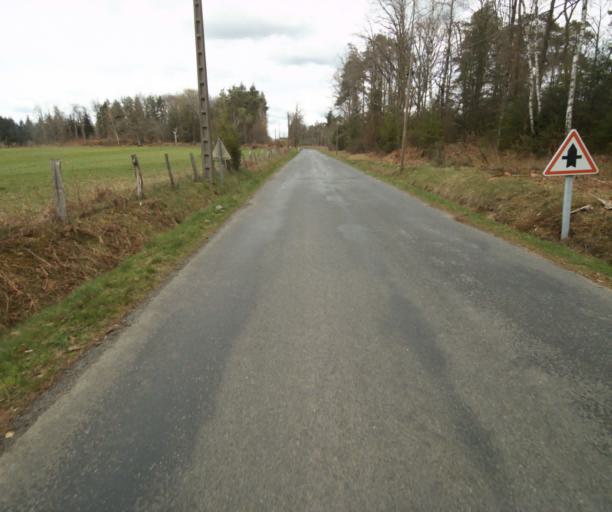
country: FR
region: Limousin
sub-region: Departement de la Correze
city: Argentat
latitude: 45.2154
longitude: 1.9260
